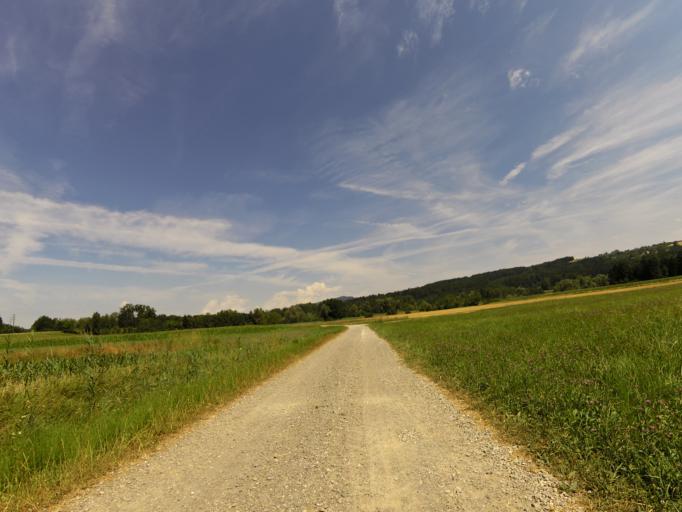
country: CH
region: Aargau
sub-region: Bezirk Bremgarten
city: Unterlunkhofen
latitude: 47.3263
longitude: 8.3588
